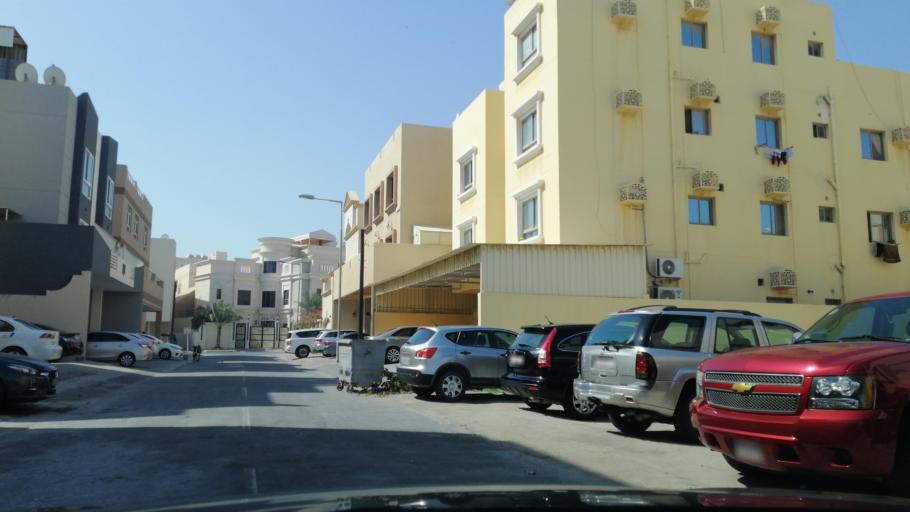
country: BH
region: Muharraq
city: Al Muharraq
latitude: 26.2455
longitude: 50.6297
